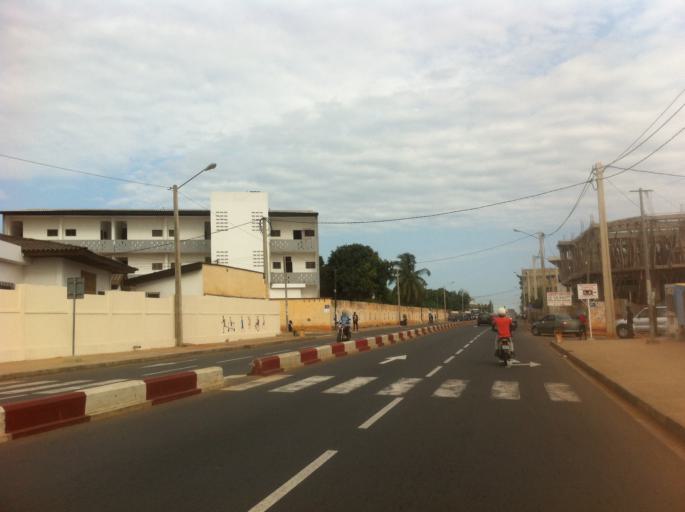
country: TG
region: Maritime
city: Lome
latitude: 6.1444
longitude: 1.2058
